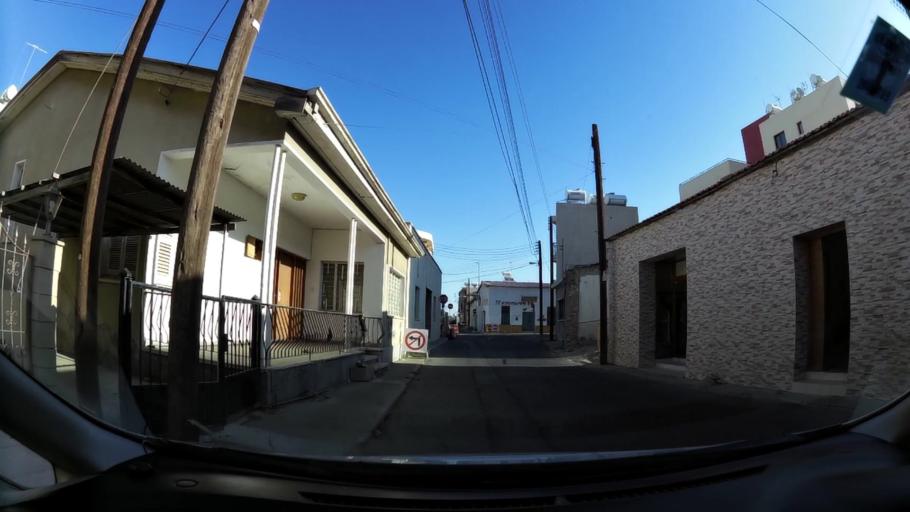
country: CY
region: Larnaka
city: Larnaca
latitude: 34.9207
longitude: 33.6202
